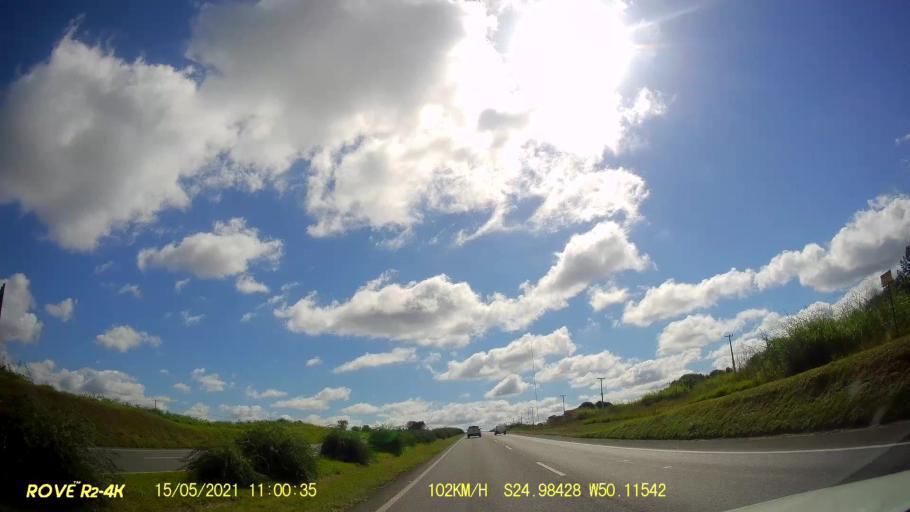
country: BR
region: Parana
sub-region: Carambei
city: Carambei
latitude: -24.9846
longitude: -50.1155
